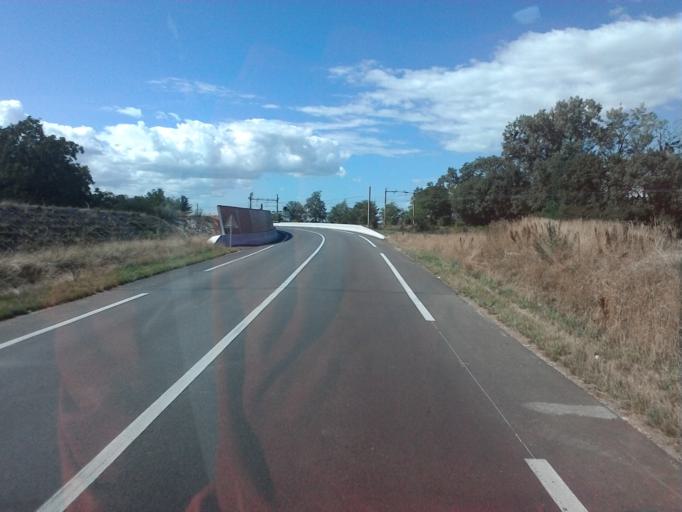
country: FR
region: Rhone-Alpes
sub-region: Departement de l'Ain
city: Ambronay
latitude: 45.9950
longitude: 5.3411
